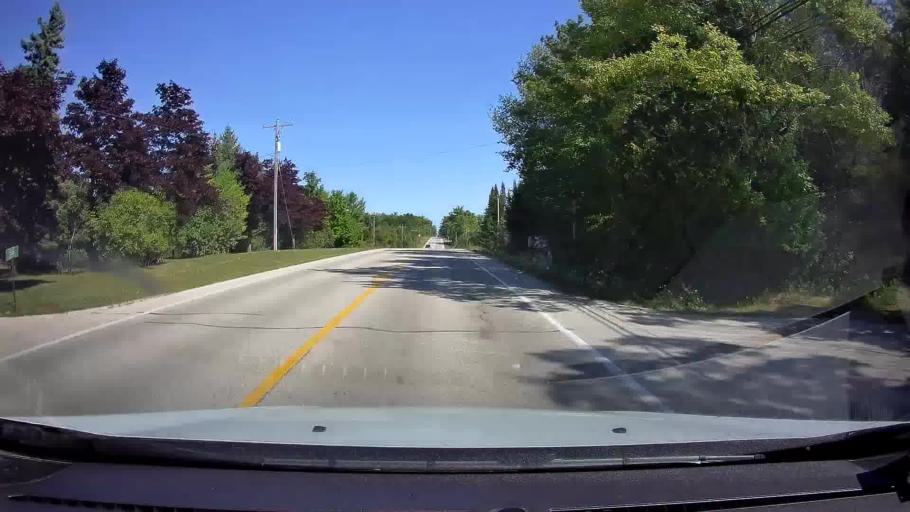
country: US
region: Michigan
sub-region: Delta County
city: Escanaba
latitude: 45.2594
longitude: -87.0456
